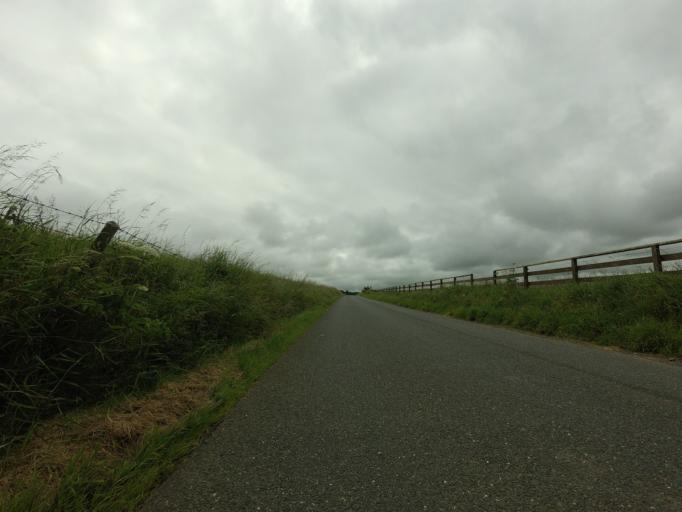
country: GB
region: Scotland
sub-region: Aberdeenshire
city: Turriff
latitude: 57.5346
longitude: -2.4264
